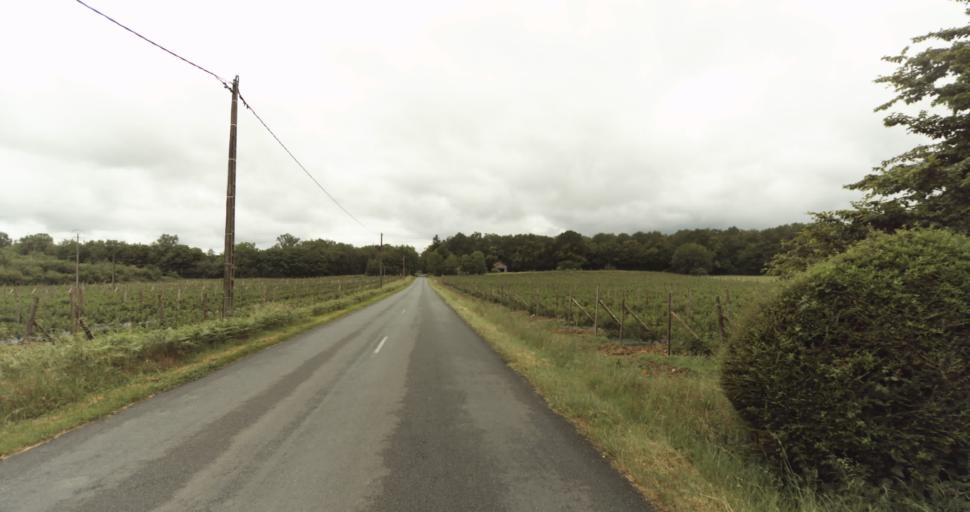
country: FR
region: Aquitaine
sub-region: Departement de la Dordogne
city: Belves
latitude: 44.6994
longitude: 0.9176
